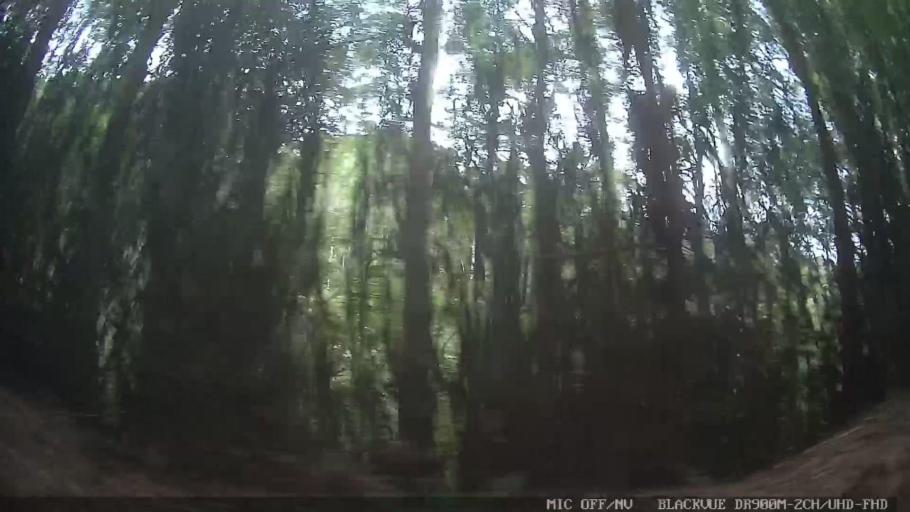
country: BR
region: Sao Paulo
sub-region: Bom Jesus Dos Perdoes
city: Bom Jesus dos Perdoes
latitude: -23.1548
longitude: -46.5110
